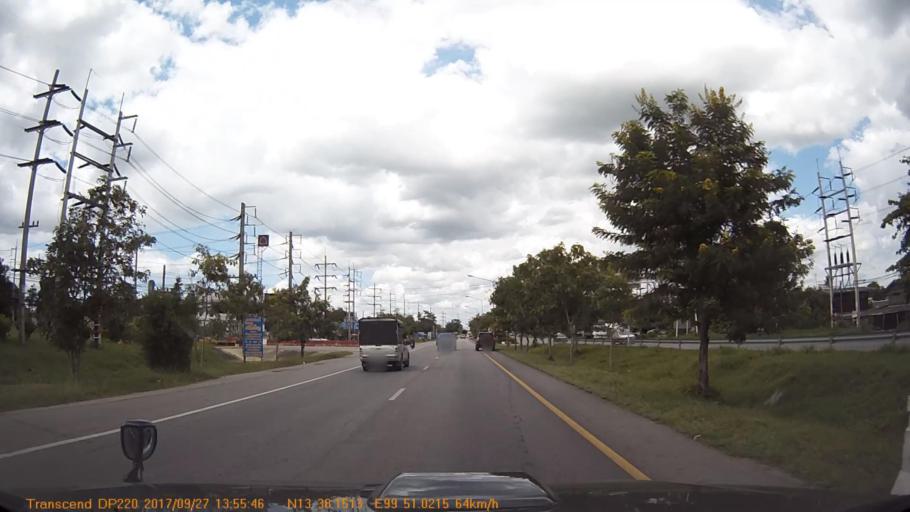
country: TH
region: Ratchaburi
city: Photharam
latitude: 13.6358
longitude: 99.8503
